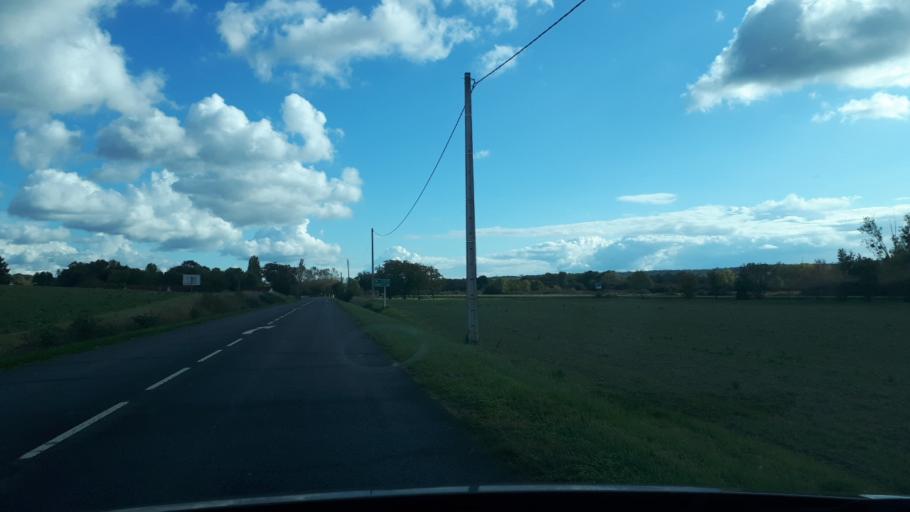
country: FR
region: Centre
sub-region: Departement du Loir-et-Cher
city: Mareuil-sur-Cher
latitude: 47.3123
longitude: 1.3354
